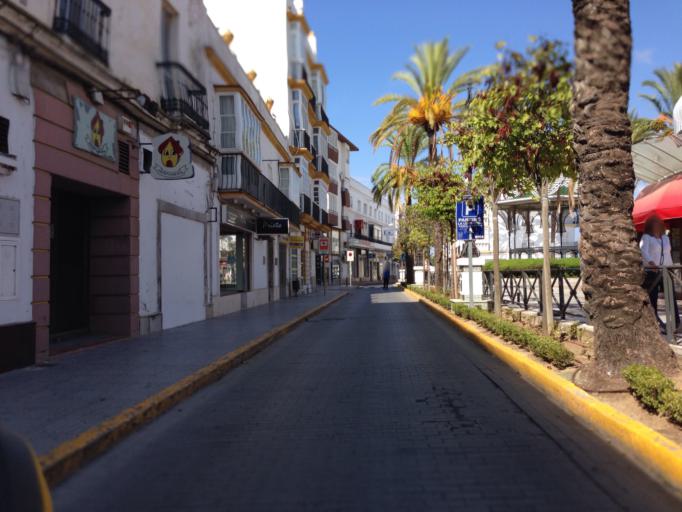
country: ES
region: Andalusia
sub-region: Provincia de Cadiz
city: Chiclana de la Frontera
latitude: 36.4213
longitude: -6.1473
